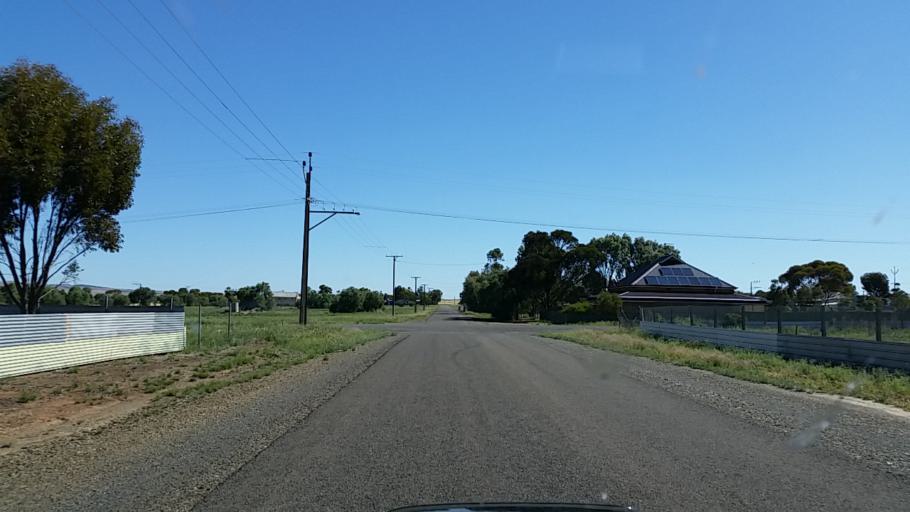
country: AU
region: South Australia
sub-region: Peterborough
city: Peterborough
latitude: -33.1518
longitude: 138.9170
